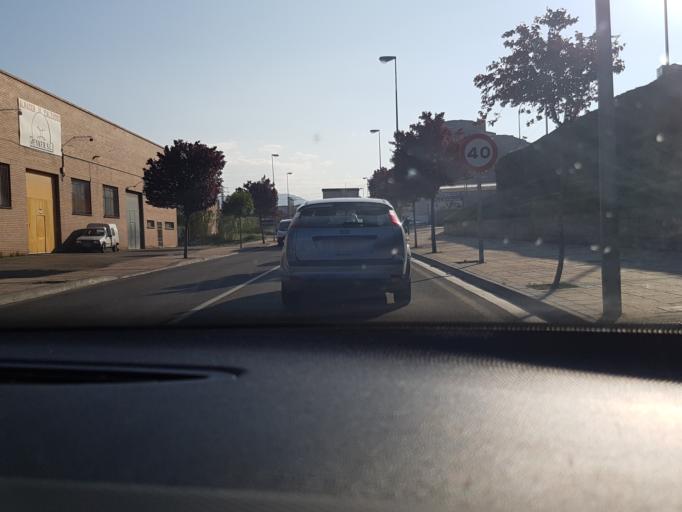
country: ES
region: La Rioja
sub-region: Provincia de La Rioja
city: Arnedo
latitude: 42.2297
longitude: -2.0883
